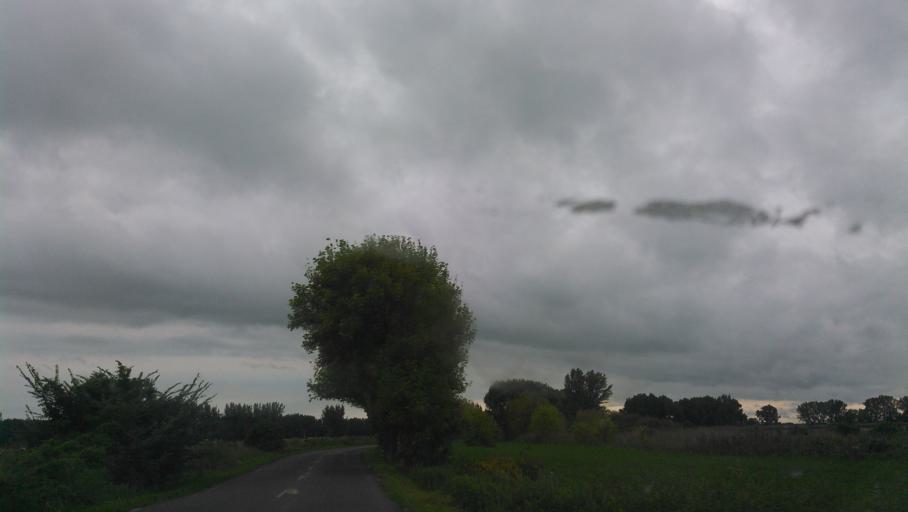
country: SK
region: Trnavsky
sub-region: Okres Dunajska Streda
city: Velky Meder
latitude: 47.9140
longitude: 17.7543
